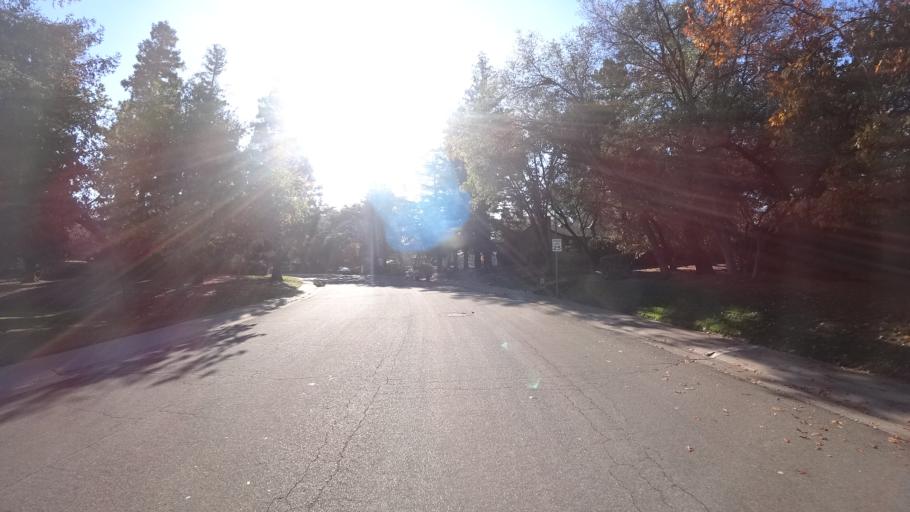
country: US
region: California
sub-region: Sacramento County
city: Citrus Heights
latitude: 38.6824
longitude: -121.3019
